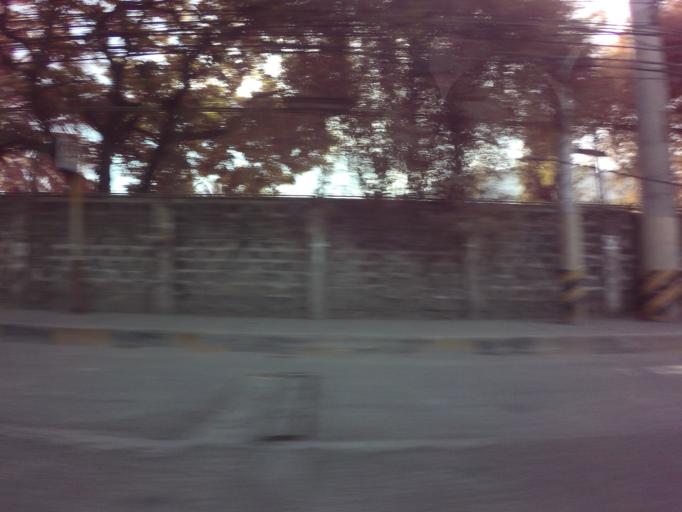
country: PH
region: Calabarzon
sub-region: Province of Rizal
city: Pateros
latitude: 14.5485
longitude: 121.0870
